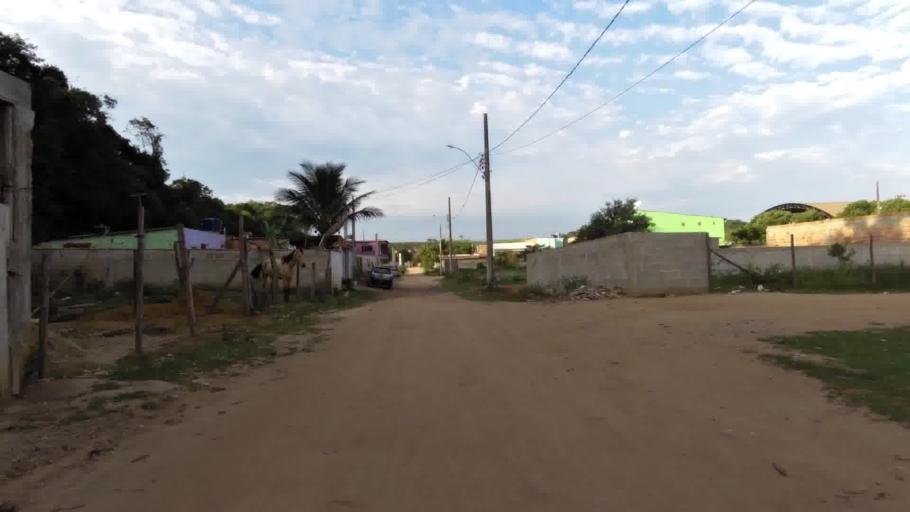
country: BR
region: Espirito Santo
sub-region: Piuma
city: Piuma
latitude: -20.8393
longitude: -40.7477
